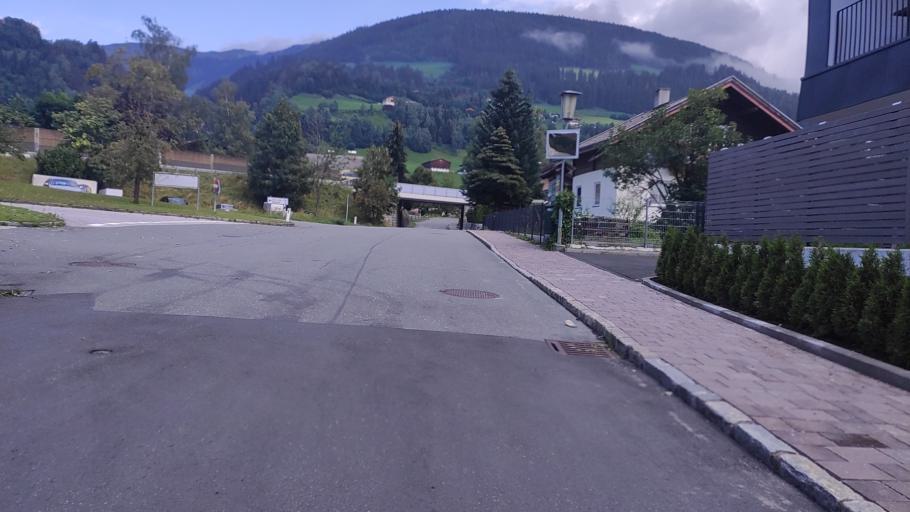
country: AT
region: Salzburg
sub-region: Politischer Bezirk Zell am See
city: Bramberg am Wildkogel
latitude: 47.2762
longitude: 12.3749
